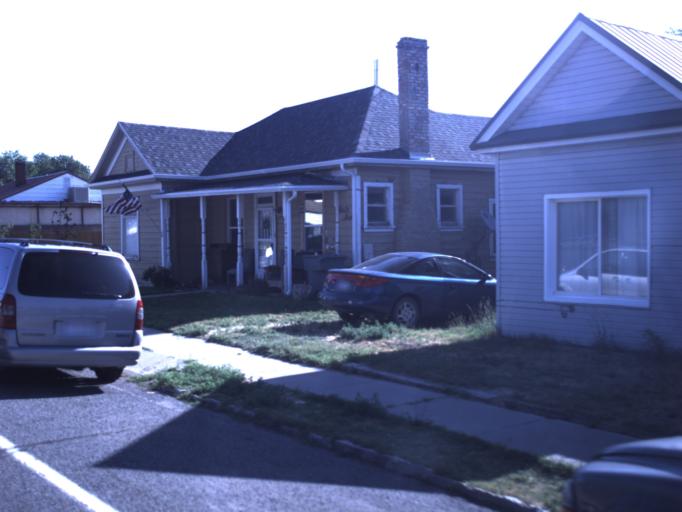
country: US
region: Utah
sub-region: Beaver County
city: Milford
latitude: 38.3994
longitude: -113.0103
